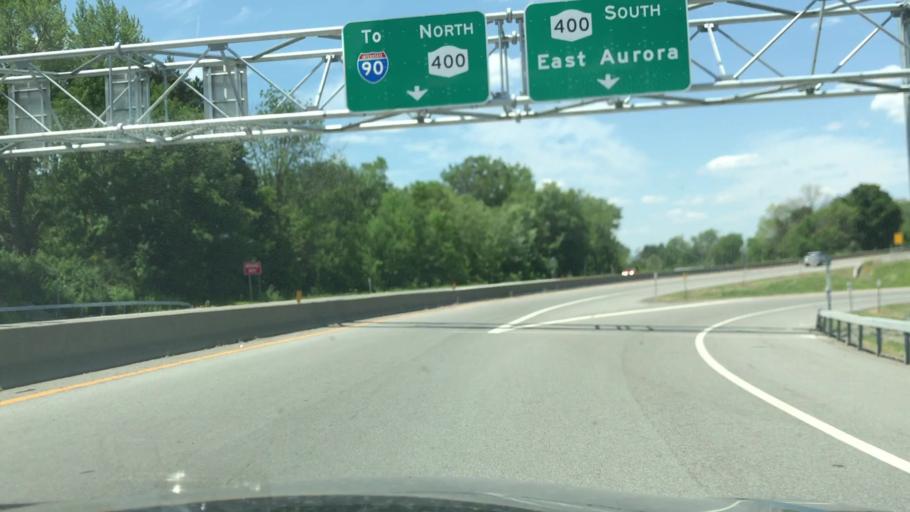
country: US
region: New York
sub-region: Erie County
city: West Seneca
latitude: 42.8420
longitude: -78.7550
